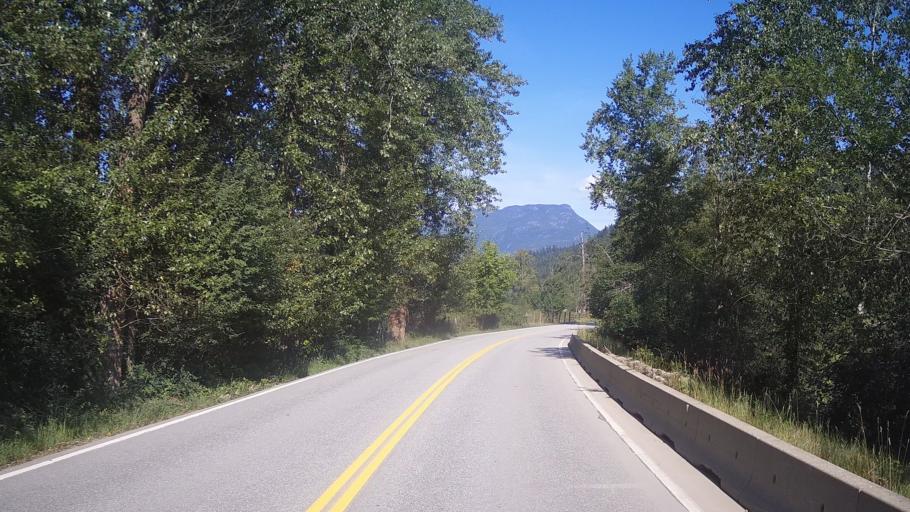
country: CA
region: British Columbia
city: Pemberton
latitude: 50.3118
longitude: -122.6745
